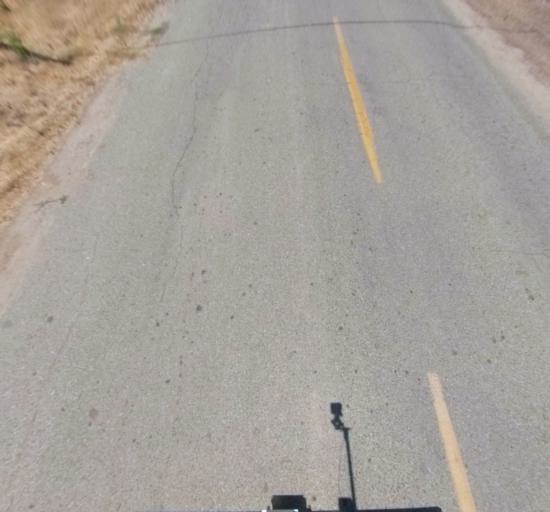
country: US
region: California
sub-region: Madera County
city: Chowchilla
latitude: 37.0910
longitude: -120.2621
